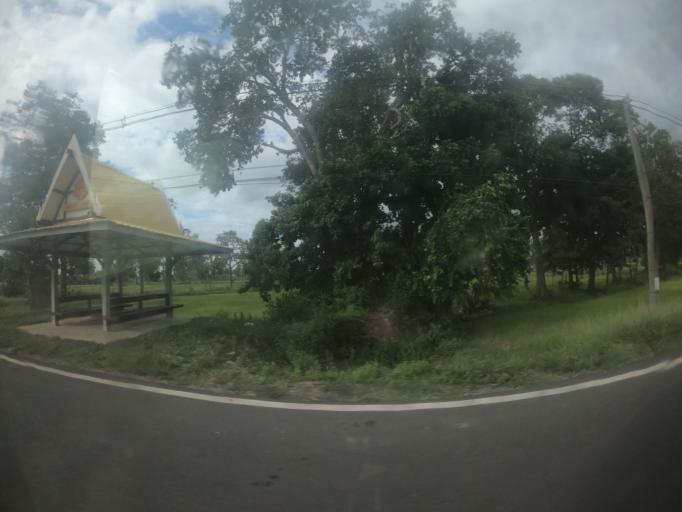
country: TH
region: Surin
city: Prasat
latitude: 14.5762
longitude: 103.4820
